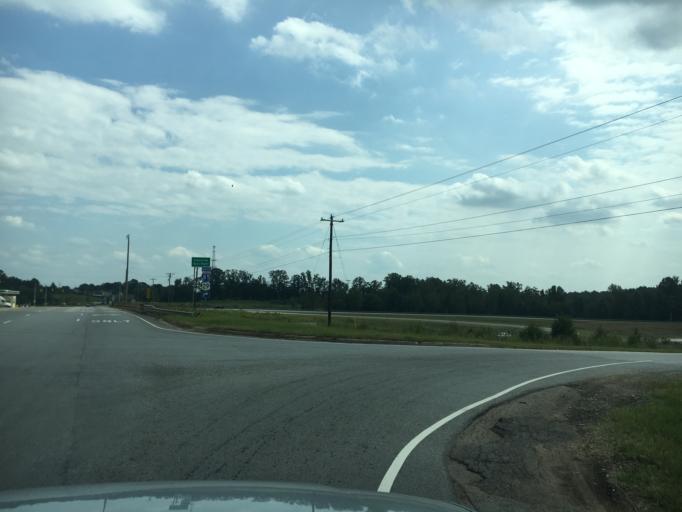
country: US
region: South Carolina
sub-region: Anderson County
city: Powdersville
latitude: 34.7756
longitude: -82.4641
